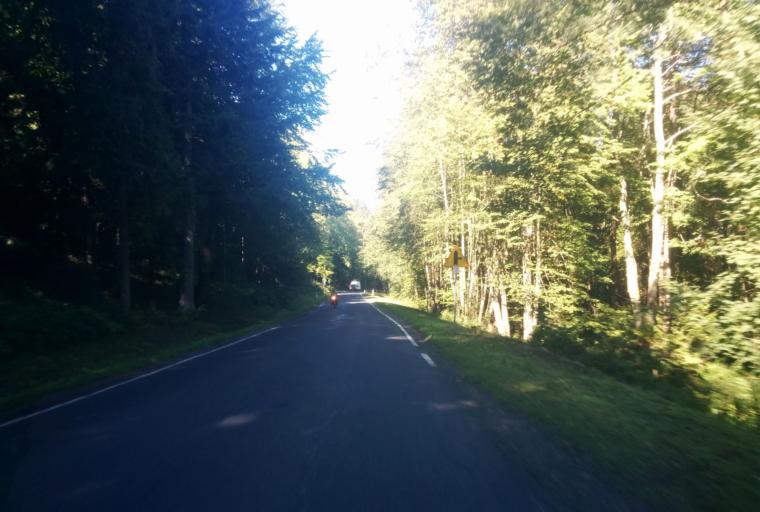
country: PL
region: Subcarpathian Voivodeship
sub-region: Powiat bieszczadzki
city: Lutowiska
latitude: 49.2878
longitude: 22.6785
